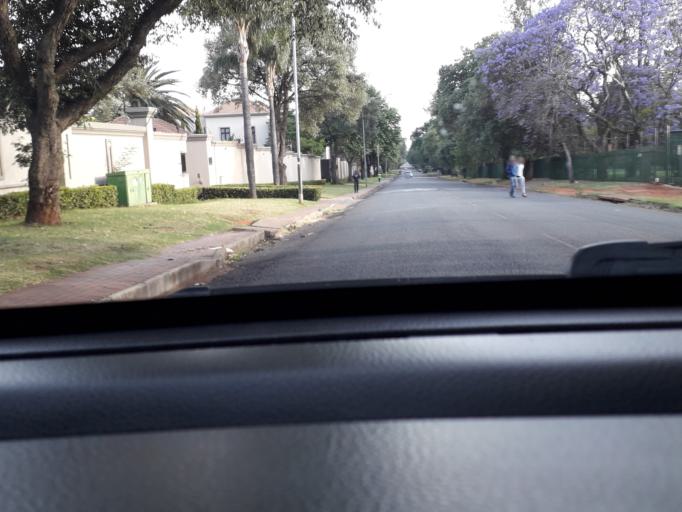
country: ZA
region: Gauteng
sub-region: City of Johannesburg Metropolitan Municipality
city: Johannesburg
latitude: -26.1672
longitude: 28.0653
